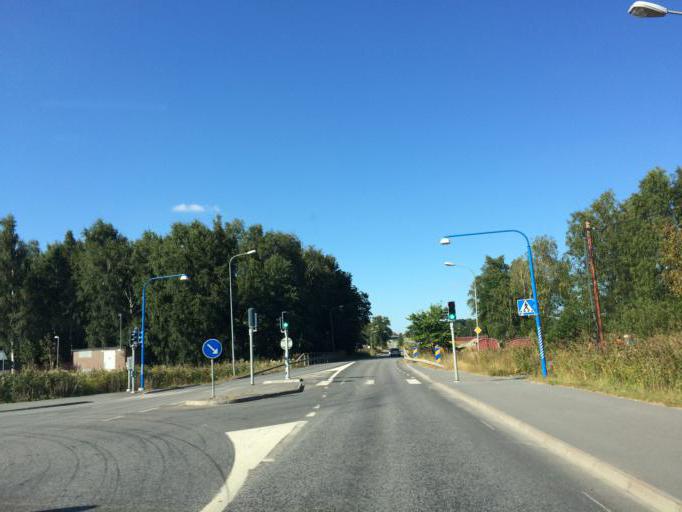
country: SE
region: Stockholm
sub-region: Upplands Vasby Kommun
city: Upplands Vaesby
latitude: 59.4790
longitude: 17.9182
